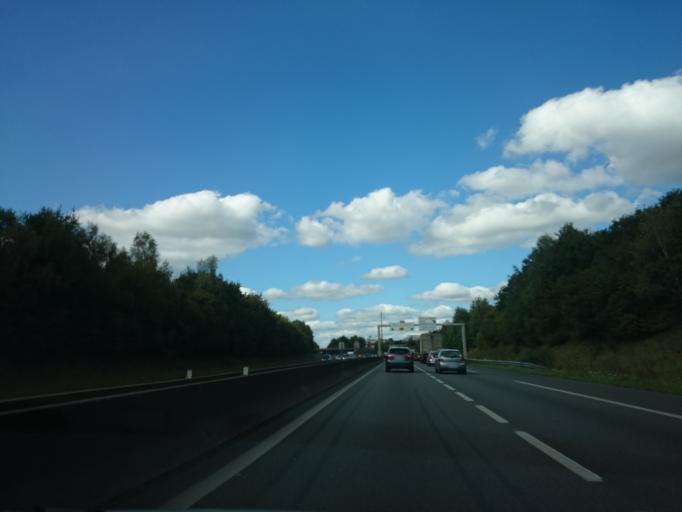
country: FR
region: Pays de la Loire
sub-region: Departement de la Loire-Atlantique
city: Orvault
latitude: 47.2472
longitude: -1.6212
